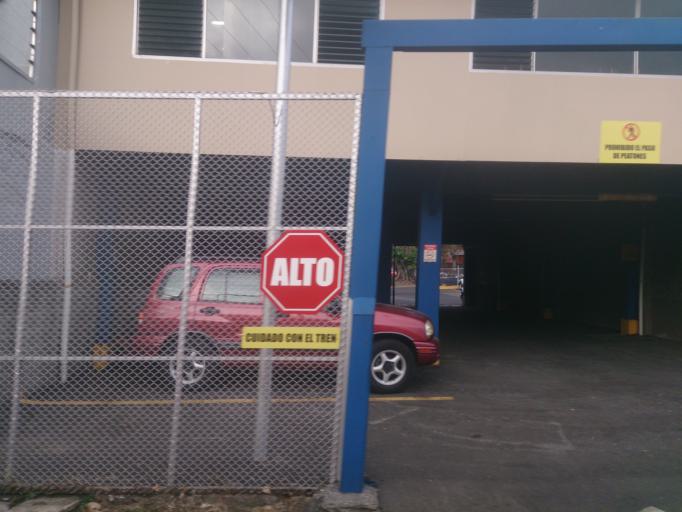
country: CR
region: San Jose
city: San Jose
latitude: 9.9323
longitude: -84.0971
